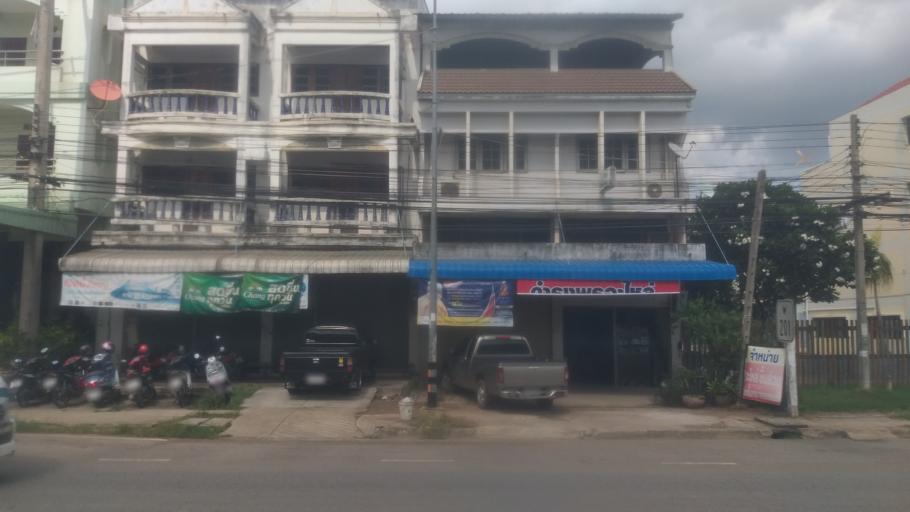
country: TH
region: Chaiyaphum
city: Chaiyaphum
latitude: 15.8010
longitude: 102.0311
